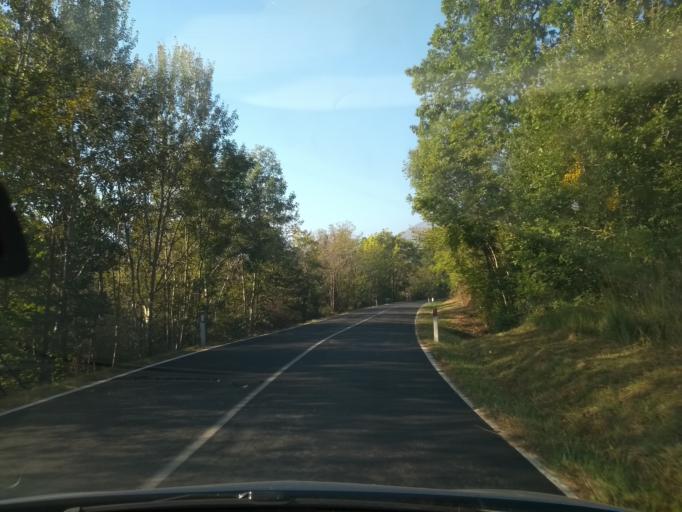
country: IT
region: Piedmont
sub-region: Provincia di Torino
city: Monasterolo
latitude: 45.2293
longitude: 7.5034
